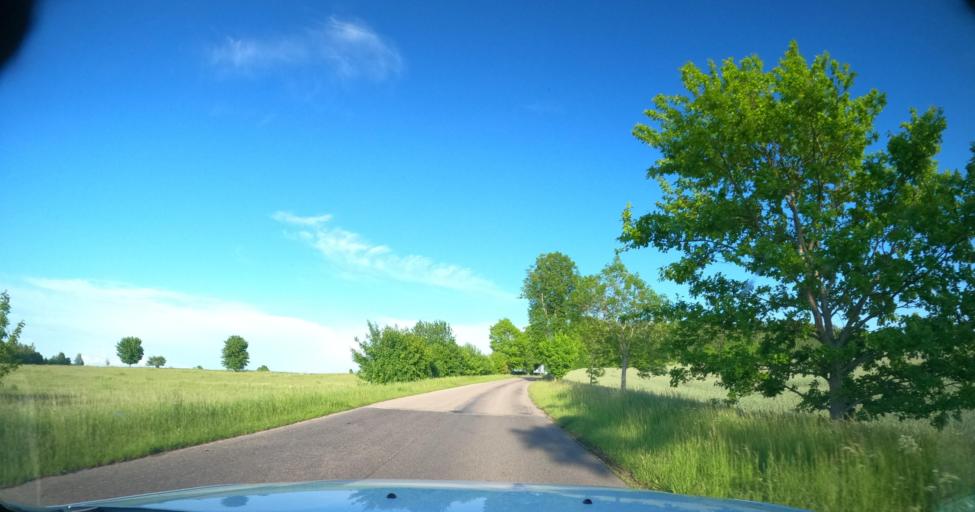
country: PL
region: Warmian-Masurian Voivodeship
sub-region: Powiat braniewski
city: Braniewo
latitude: 54.2678
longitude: 19.9410
